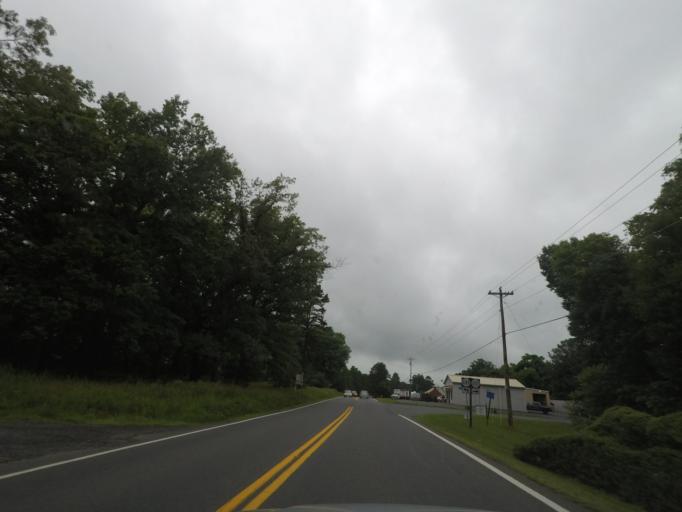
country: US
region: Virginia
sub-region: Fluvanna County
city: Palmyra
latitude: 37.9031
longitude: -78.2566
